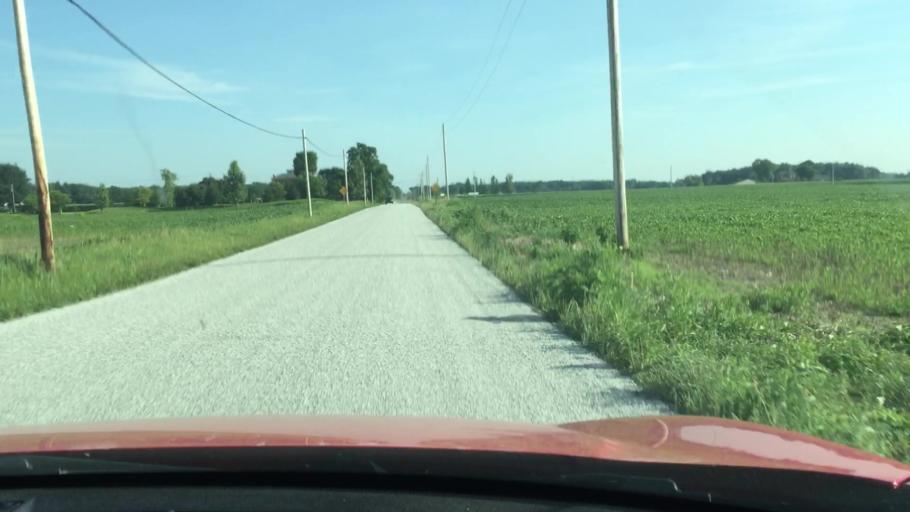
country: US
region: Ohio
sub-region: Hardin County
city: Ada
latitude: 40.7484
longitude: -83.8424
